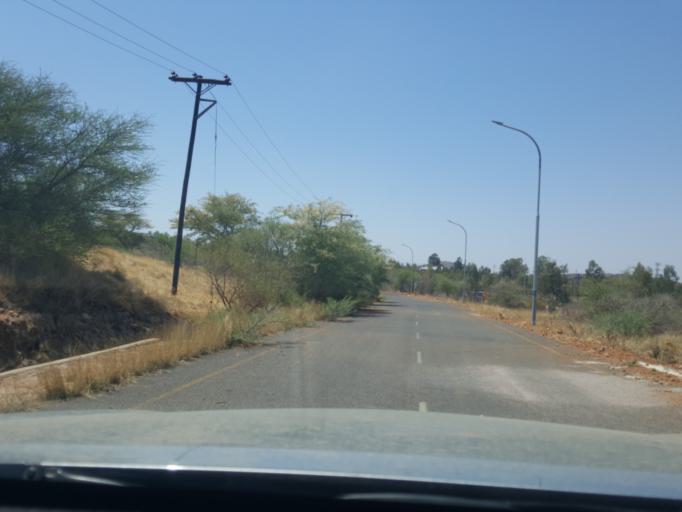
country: BW
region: South East
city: Lobatse
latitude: -25.1854
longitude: 25.6797
